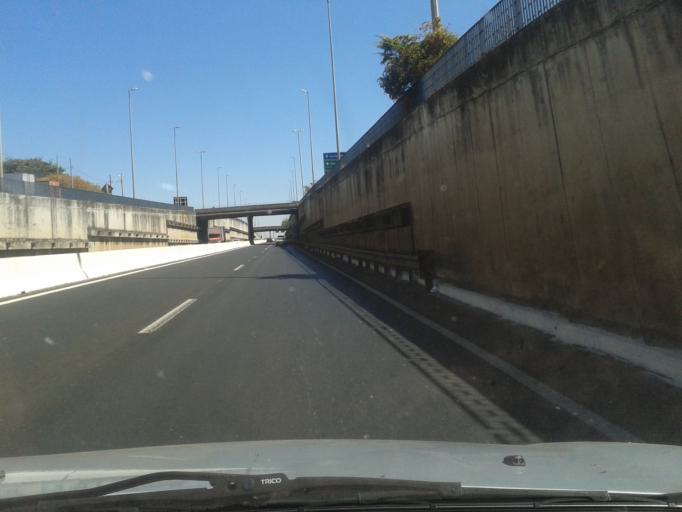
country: BR
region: Minas Gerais
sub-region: Uberlandia
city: Uberlandia
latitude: -18.8998
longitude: -48.2406
